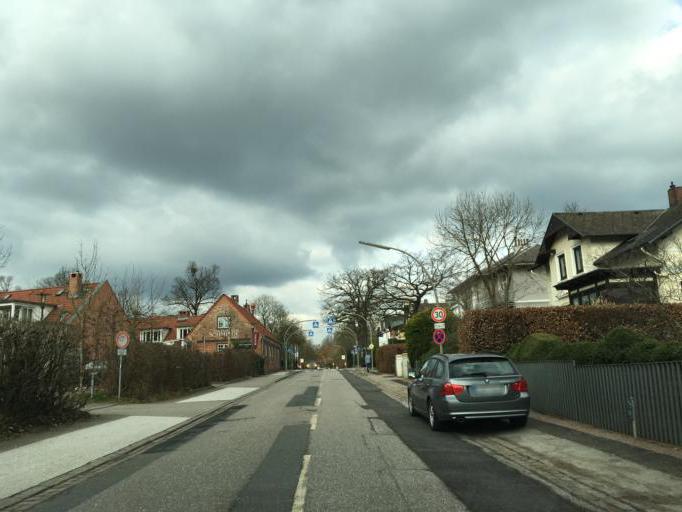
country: DE
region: Hamburg
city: Eidelstedt
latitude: 53.5562
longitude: 9.8651
